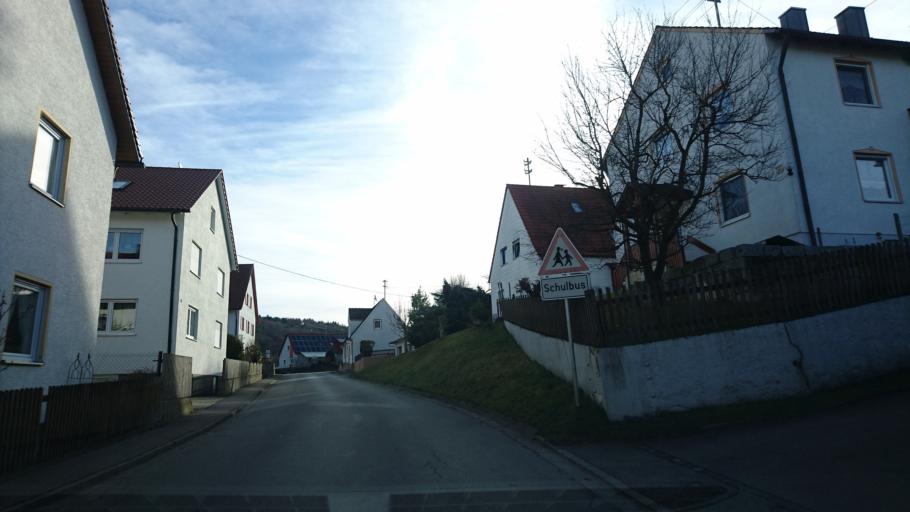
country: DE
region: Bavaria
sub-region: Swabia
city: Altenmunster
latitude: 48.4610
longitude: 10.5988
